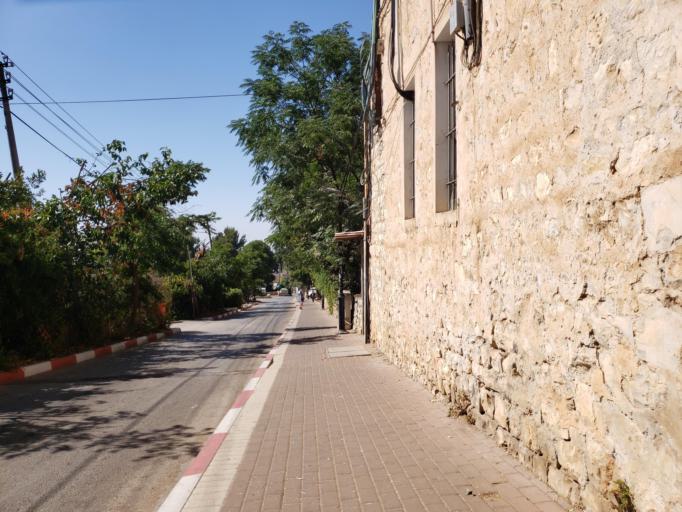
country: IL
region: Northern District
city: Safed
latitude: 32.9614
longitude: 35.4974
